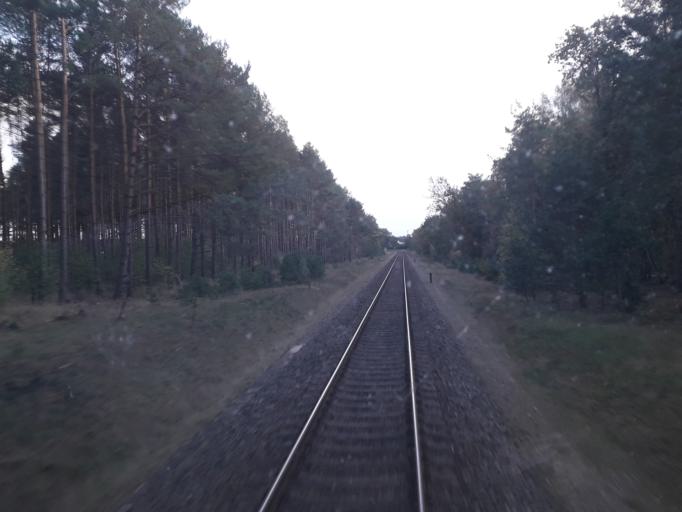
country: DE
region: Brandenburg
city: Wittstock
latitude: 53.0764
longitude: 12.5370
